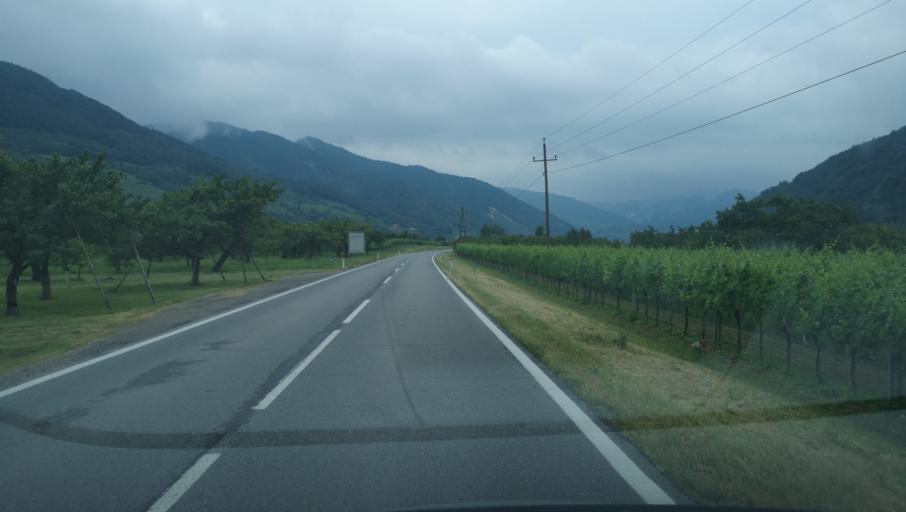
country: AT
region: Lower Austria
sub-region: Politischer Bezirk Krems
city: Aggsbach
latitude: 48.3253
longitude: 15.4070
